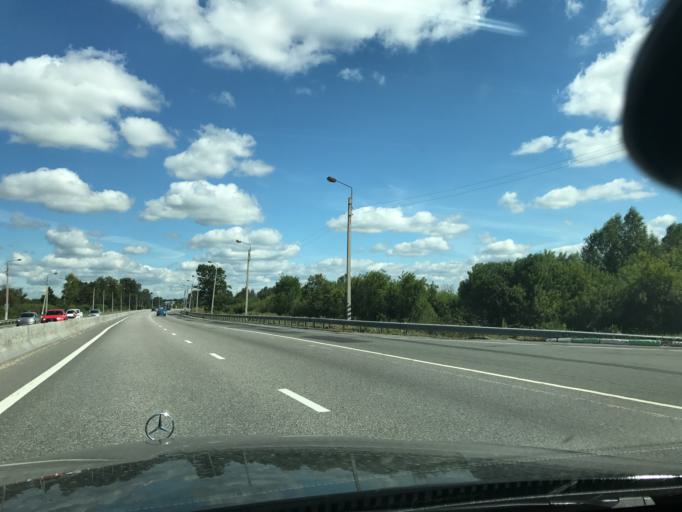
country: RU
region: Nizjnij Novgorod
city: Mulino
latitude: 56.2745
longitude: 42.9664
